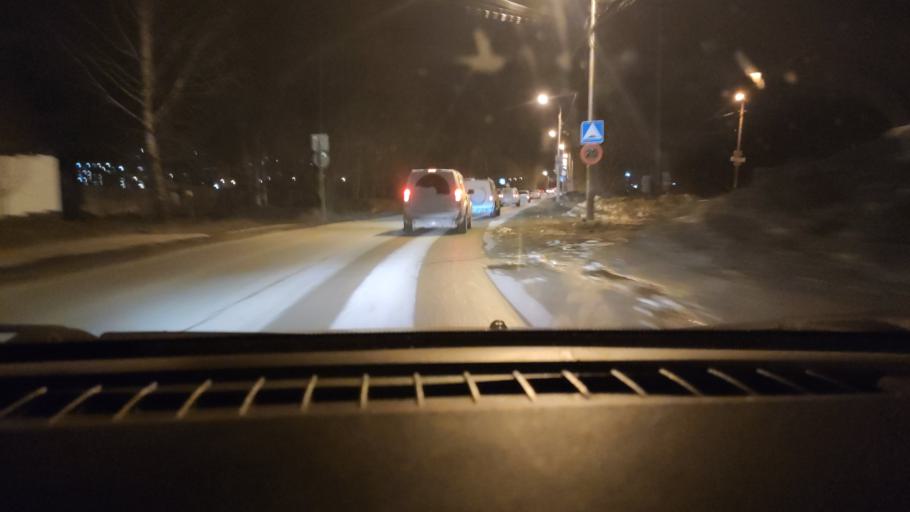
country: RU
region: Perm
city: Perm
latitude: 58.0479
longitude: 56.3390
